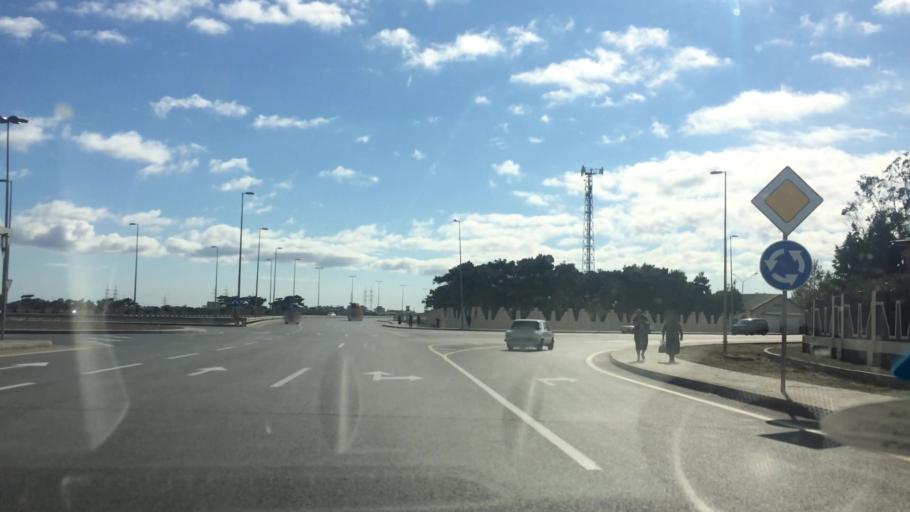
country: AZ
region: Baki
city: Qala
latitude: 40.4444
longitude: 50.1761
